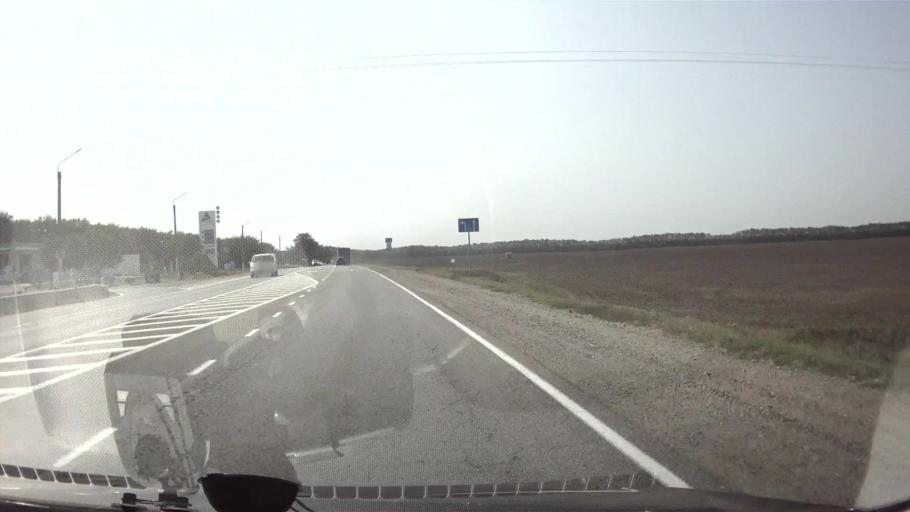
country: RU
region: Adygeya
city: Krasnogvardeyskoye
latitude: 45.2060
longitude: 39.5416
